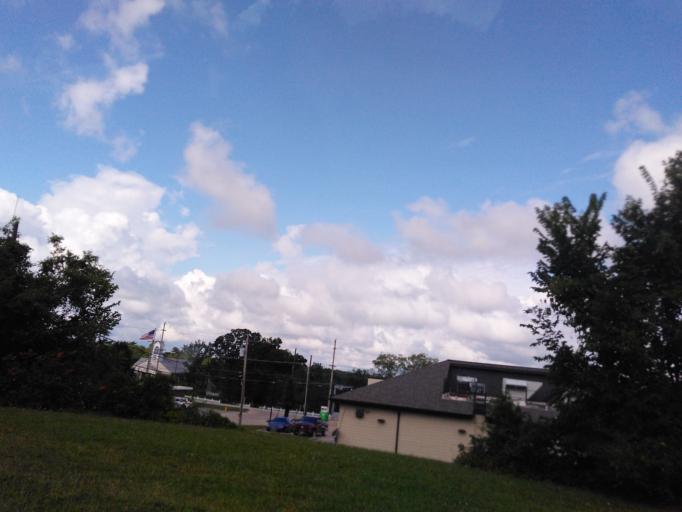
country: US
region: Missouri
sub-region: Jefferson County
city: Hillsboro
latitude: 38.2346
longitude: -90.5610
